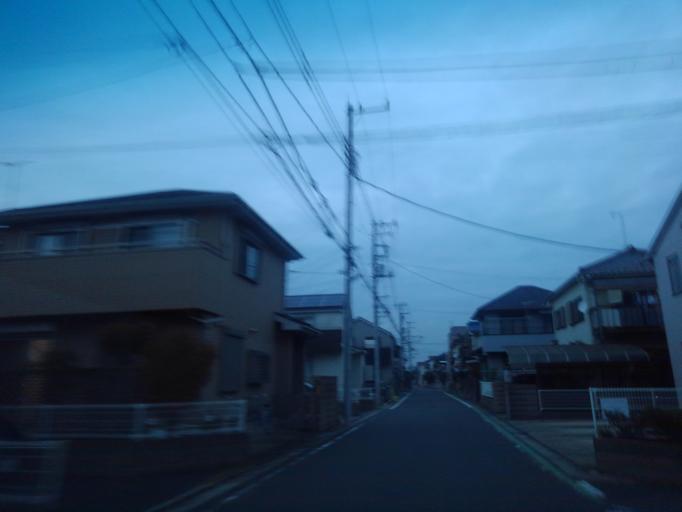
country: JP
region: Saitama
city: Tokorozawa
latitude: 35.7997
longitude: 139.4450
